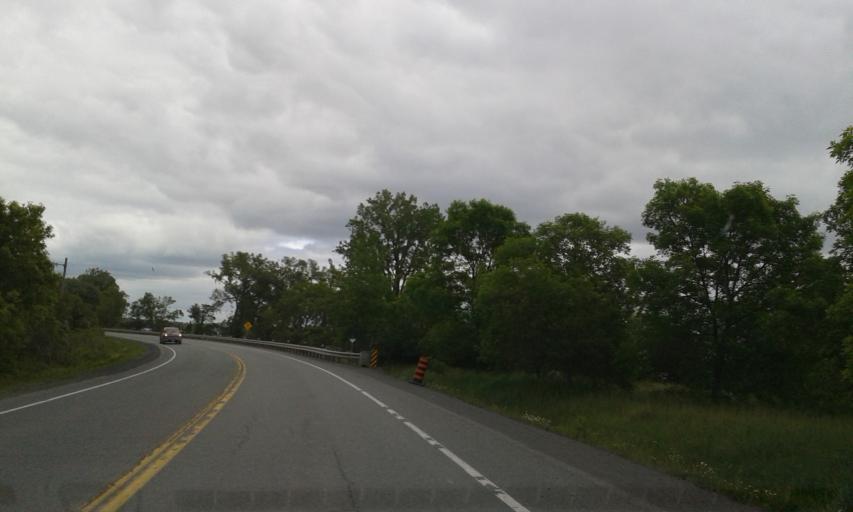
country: CA
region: Ontario
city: Skatepark
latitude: 44.1673
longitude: -76.7948
